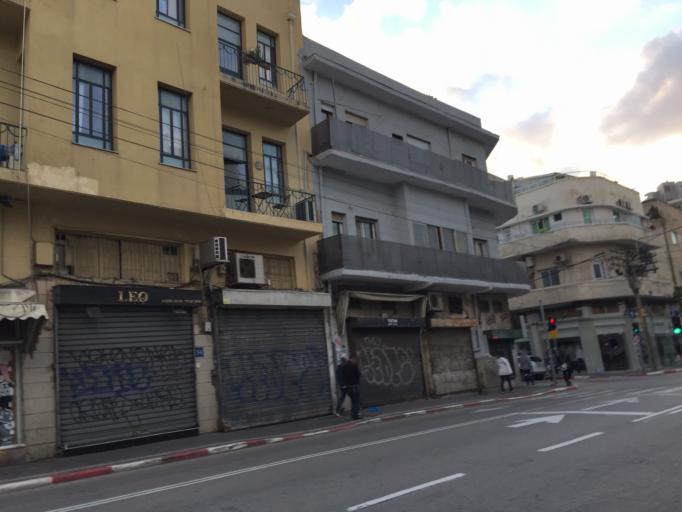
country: IL
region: Tel Aviv
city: Tel Aviv
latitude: 32.0606
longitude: 34.7731
